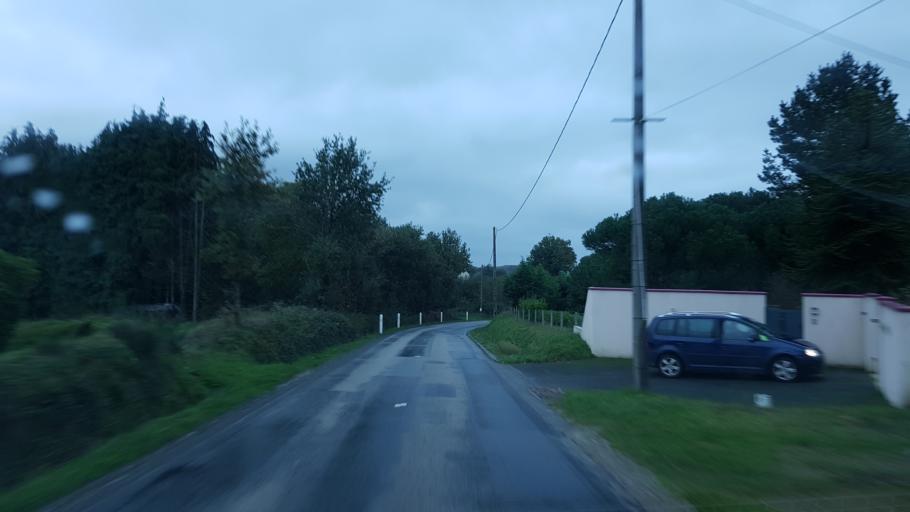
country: FR
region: Brittany
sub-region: Departement du Morbihan
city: Sulniac
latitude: 47.6893
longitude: -2.5732
